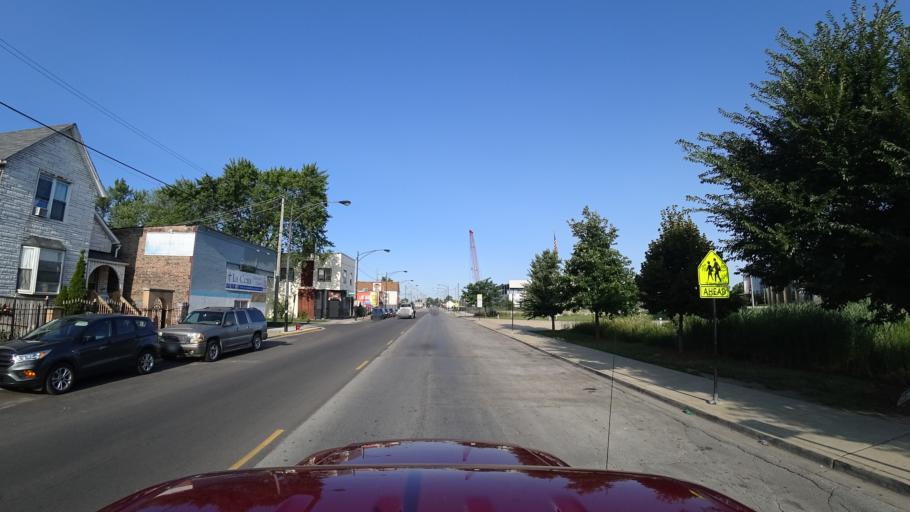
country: US
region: Illinois
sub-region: Cook County
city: Cicero
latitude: 41.8007
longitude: -87.7095
